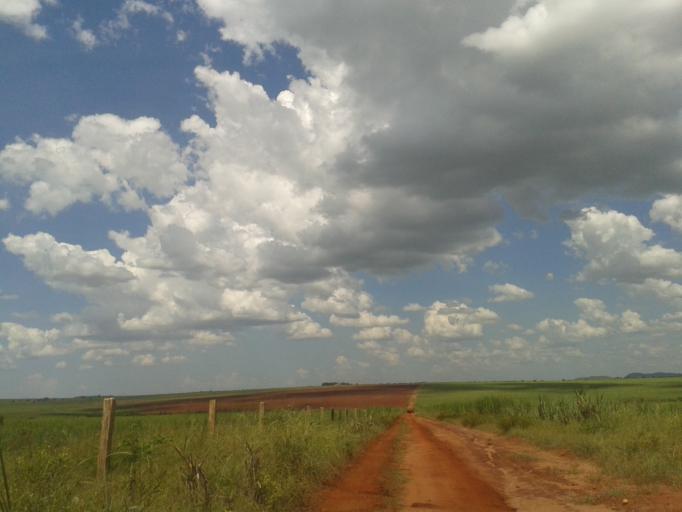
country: BR
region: Minas Gerais
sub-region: Santa Vitoria
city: Santa Vitoria
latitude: -19.1780
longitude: -50.4428
